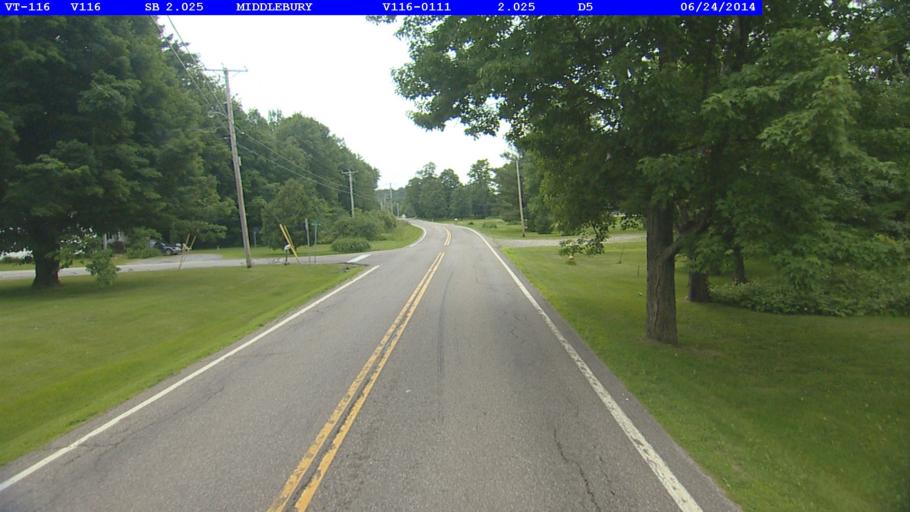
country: US
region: Vermont
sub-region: Addison County
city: Middlebury (village)
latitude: 43.9937
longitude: -73.1050
